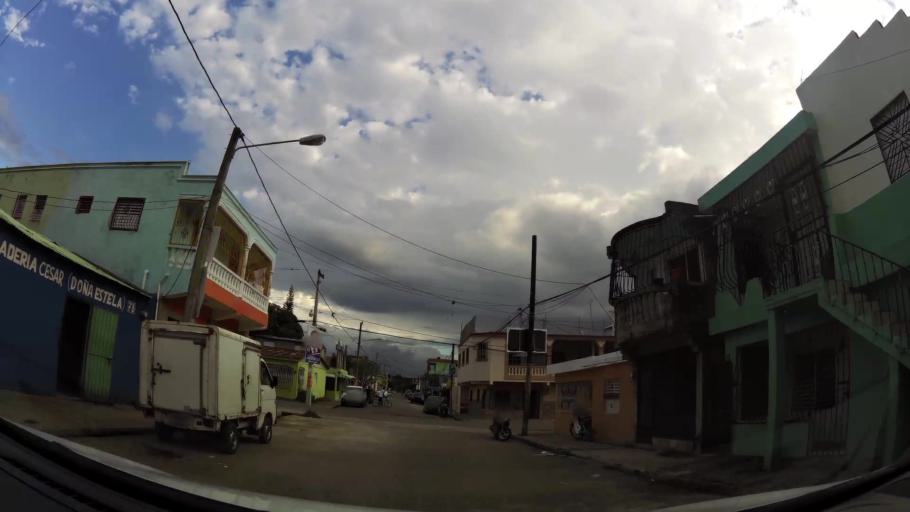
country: DO
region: San Cristobal
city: Villa Altagracia
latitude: 18.6742
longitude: -70.1740
